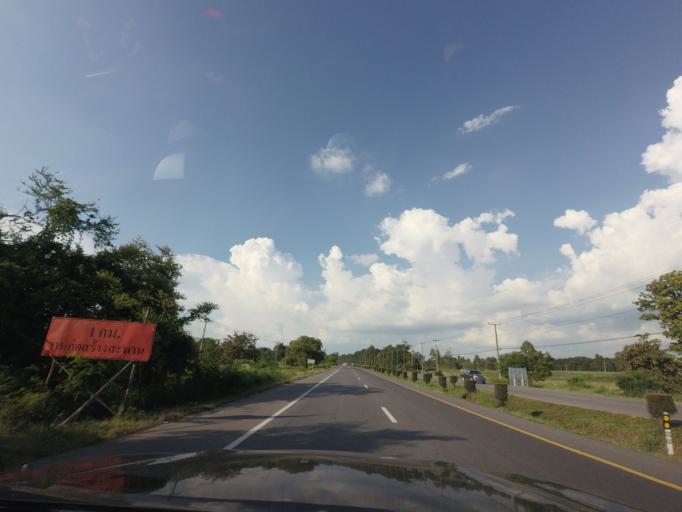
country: TH
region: Khon Kaen
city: Ban Haet
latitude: 16.1343
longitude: 102.7465
